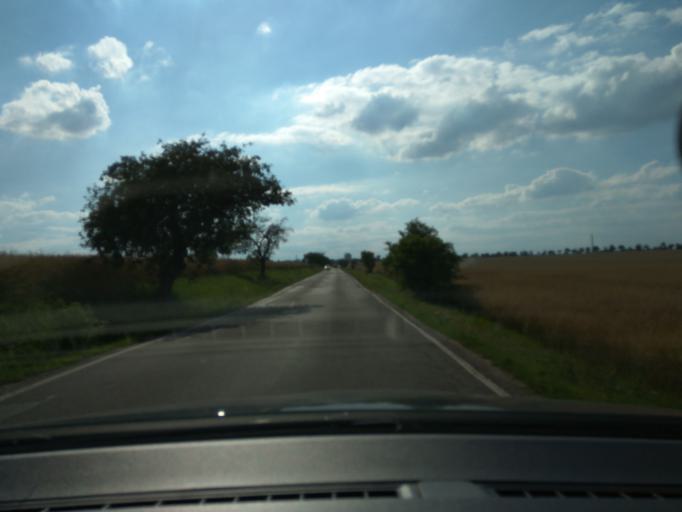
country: CZ
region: Praha
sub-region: Praha 19
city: Kbely
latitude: 50.1468
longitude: 14.5561
